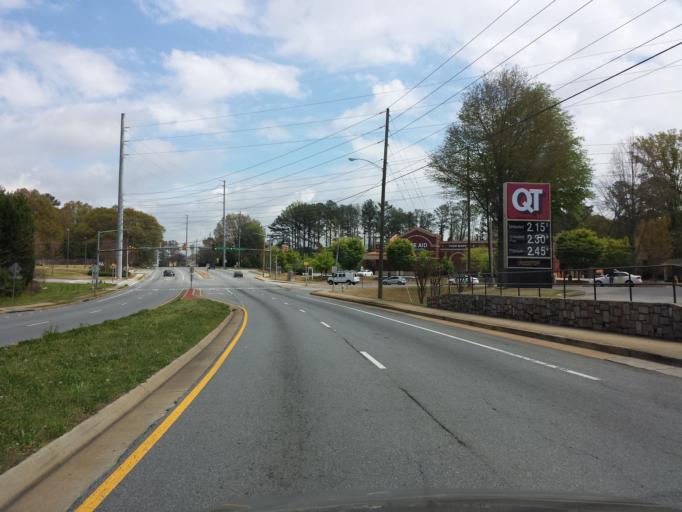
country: US
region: Georgia
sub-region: Cobb County
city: Marietta
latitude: 33.9951
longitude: -84.5089
